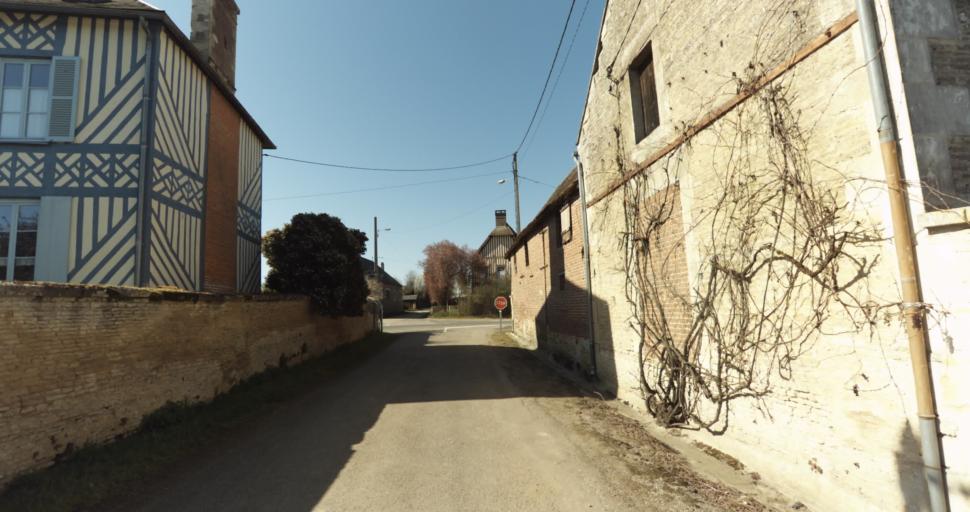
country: FR
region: Lower Normandy
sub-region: Departement du Calvados
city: Saint-Pierre-sur-Dives
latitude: 48.9753
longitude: 0.0386
